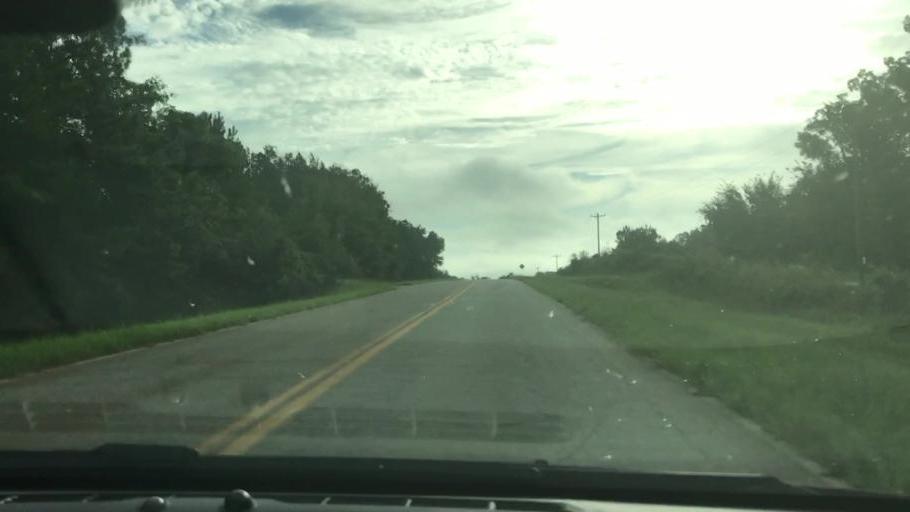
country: US
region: Georgia
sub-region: Quitman County
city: Georgetown
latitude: 31.8951
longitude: -85.0606
